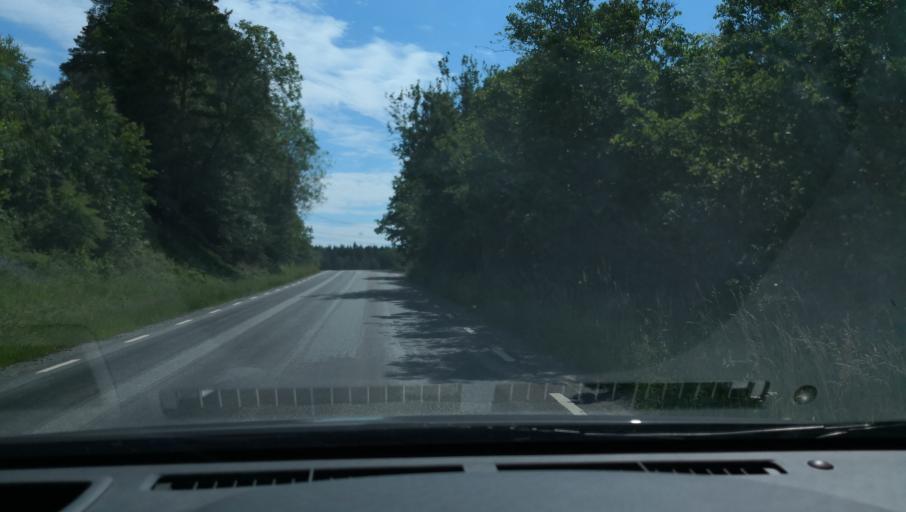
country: SE
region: Uppsala
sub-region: Habo Kommun
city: Balsta
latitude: 59.6601
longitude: 17.4507
